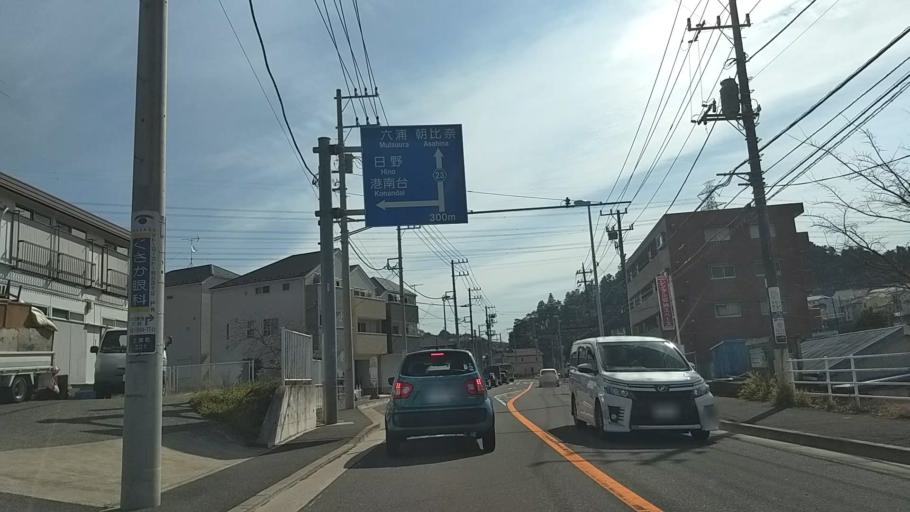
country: JP
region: Kanagawa
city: Kamakura
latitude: 35.3640
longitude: 139.5719
